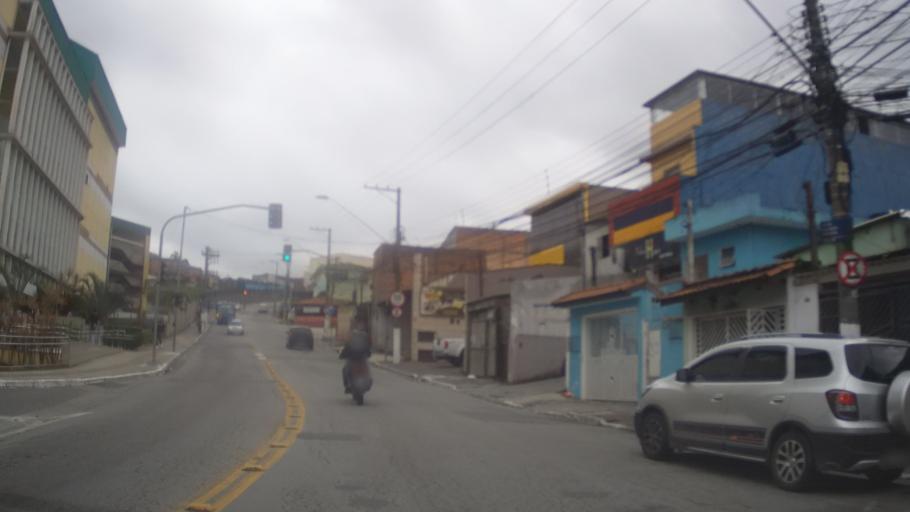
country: BR
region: Sao Paulo
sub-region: Guarulhos
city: Guarulhos
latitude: -23.4293
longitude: -46.5367
